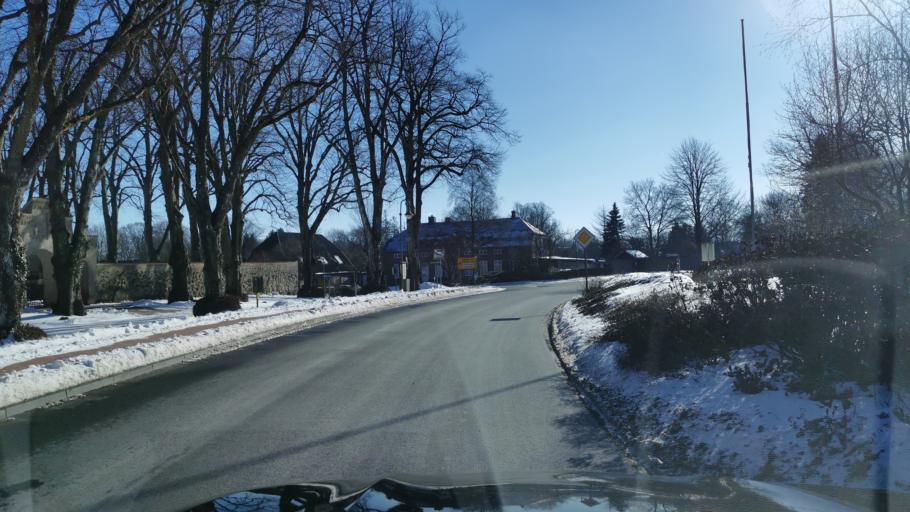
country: DE
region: Schleswig-Holstein
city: Grundhof
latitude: 54.7739
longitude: 9.6530
